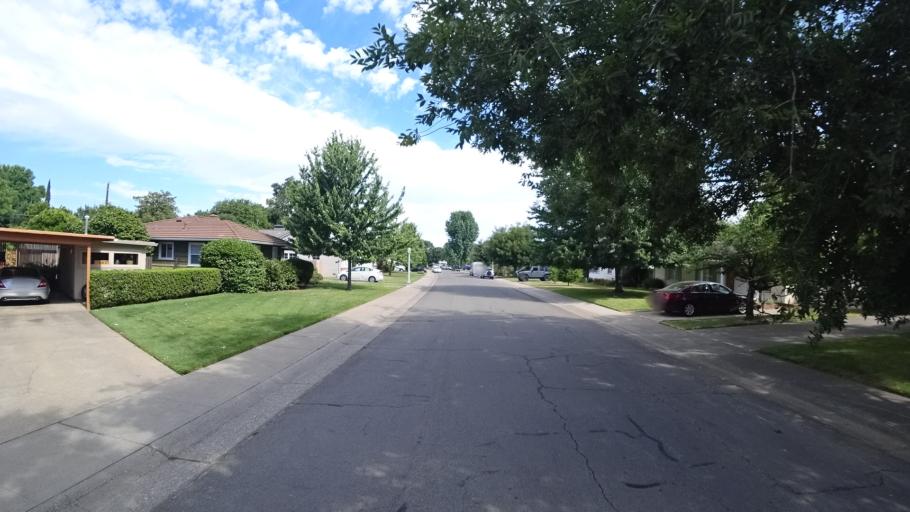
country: US
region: California
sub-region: Sacramento County
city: Arden-Arcade
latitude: 38.5737
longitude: -121.4262
